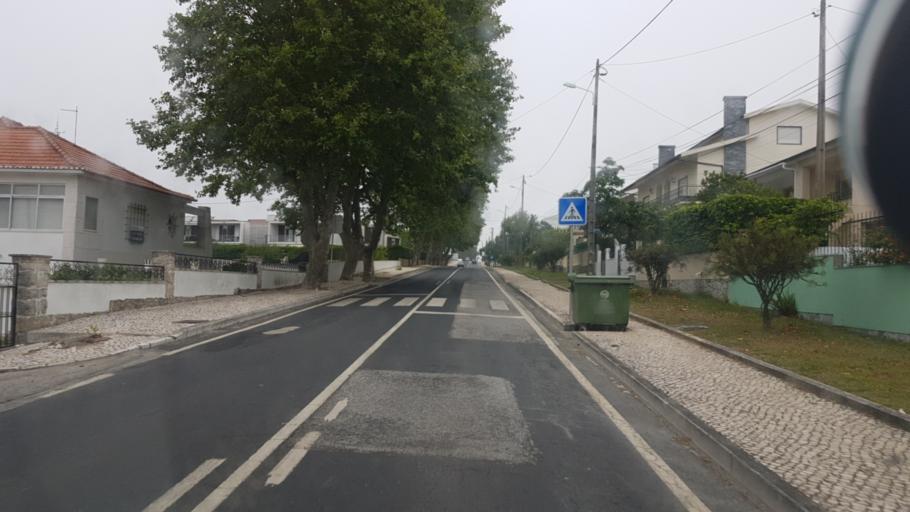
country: PT
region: Lisbon
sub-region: Sintra
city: Sintra
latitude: 38.8130
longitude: -9.3697
